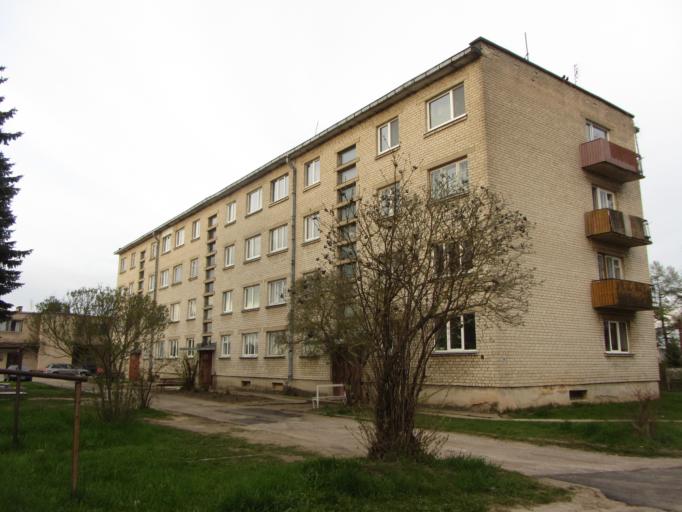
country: LT
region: Utenos apskritis
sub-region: Utena
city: Utena
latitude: 55.7380
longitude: 25.8330
